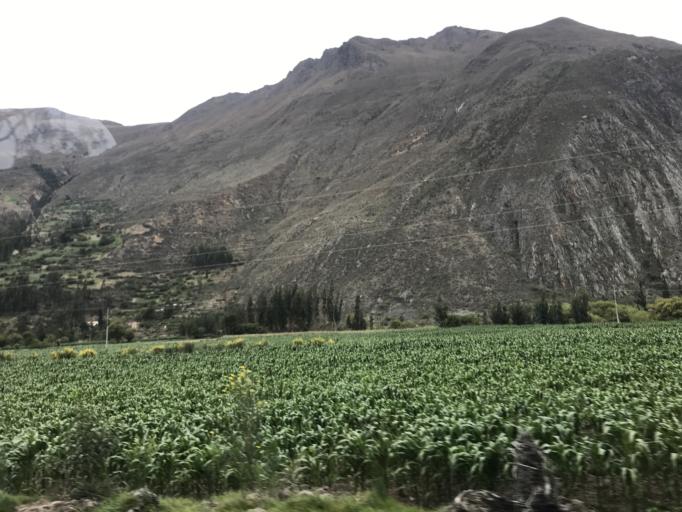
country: PE
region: Cusco
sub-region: Provincia de Urubamba
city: Ollantaytambo
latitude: -13.2446
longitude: -72.2939
